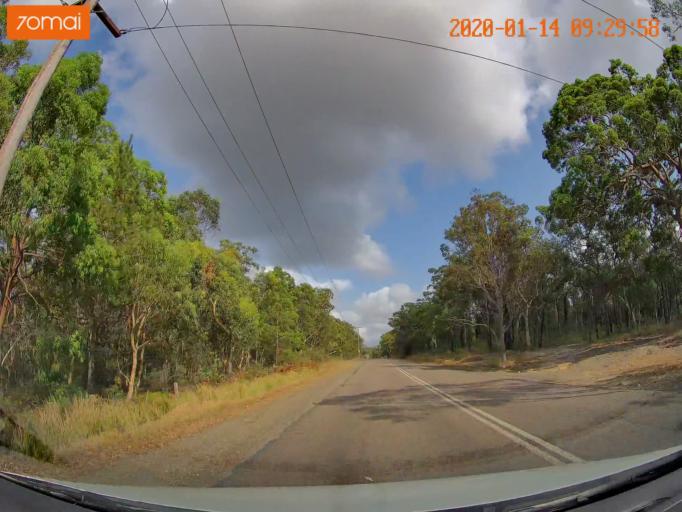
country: AU
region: New South Wales
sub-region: Lake Macquarie Shire
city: Dora Creek
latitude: -33.1195
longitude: 151.5215
